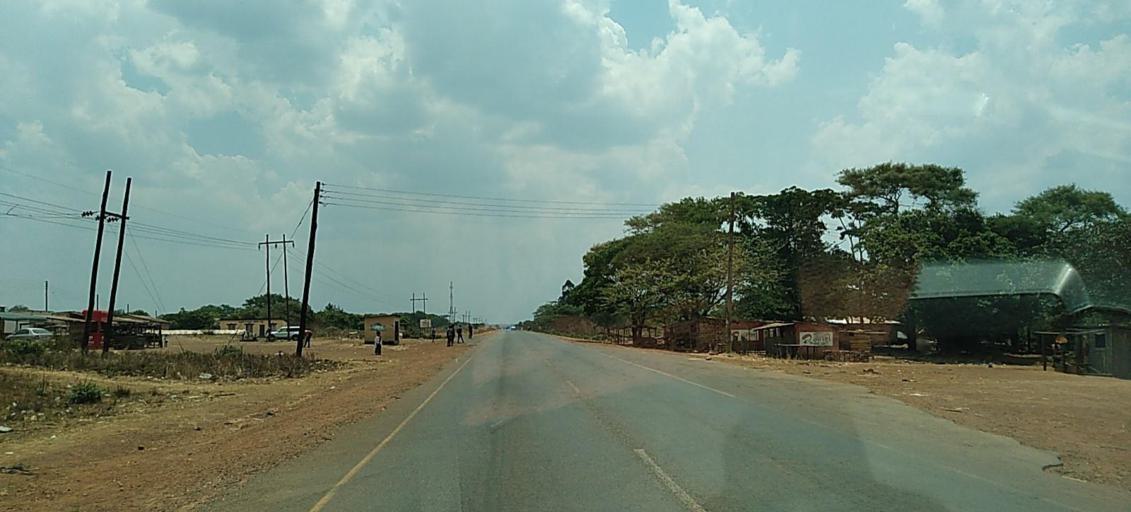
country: ZM
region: Copperbelt
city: Kalulushi
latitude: -12.8383
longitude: 27.9886
